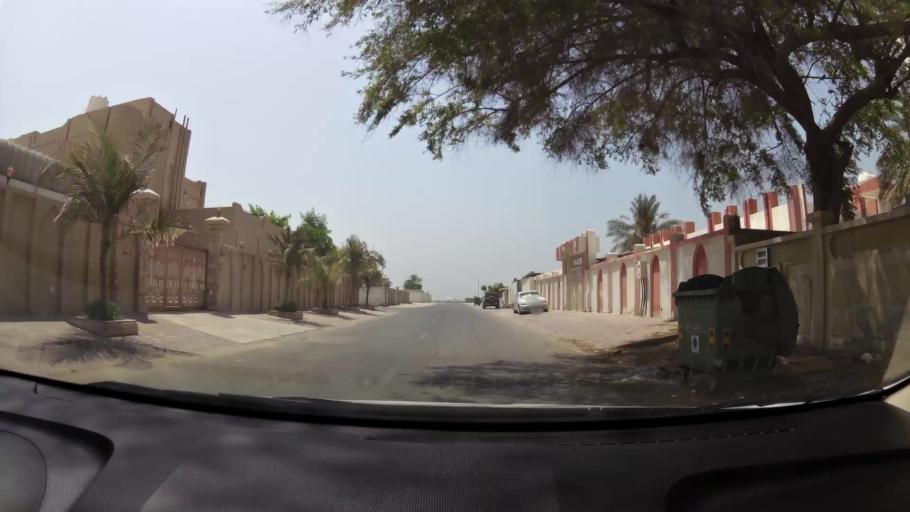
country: AE
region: Ajman
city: Ajman
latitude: 25.3980
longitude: 55.4277
